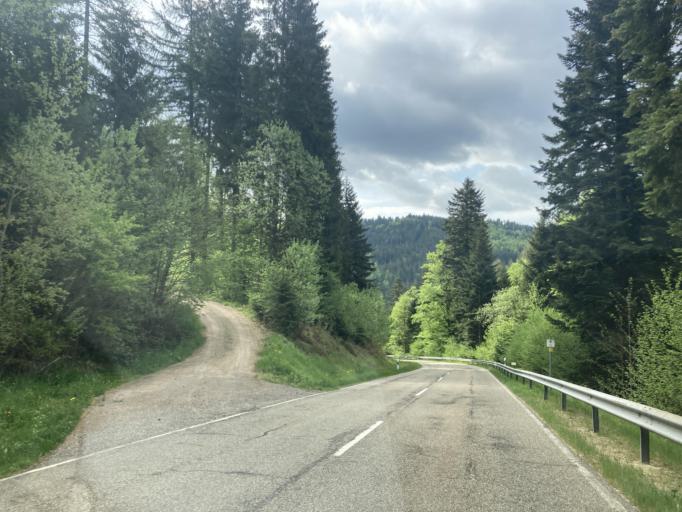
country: DE
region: Baden-Wuerttemberg
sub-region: Karlsruhe Region
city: Forbach
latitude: 48.6424
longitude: 8.3378
